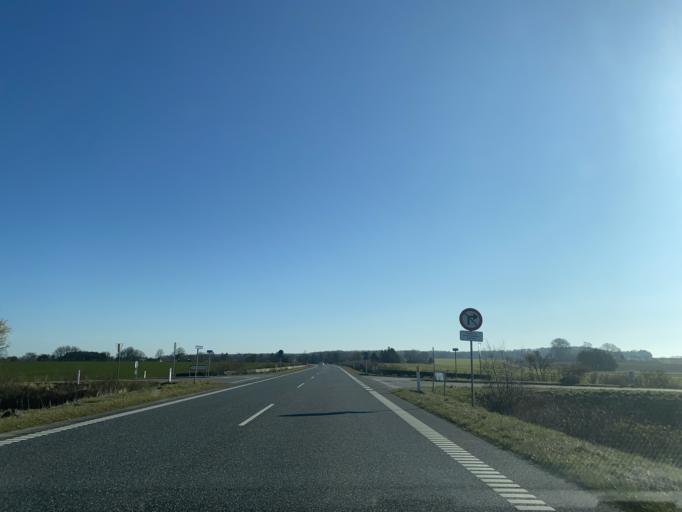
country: DK
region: Central Jutland
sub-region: Favrskov Kommune
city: Ulstrup
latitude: 56.3192
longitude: 9.7926
